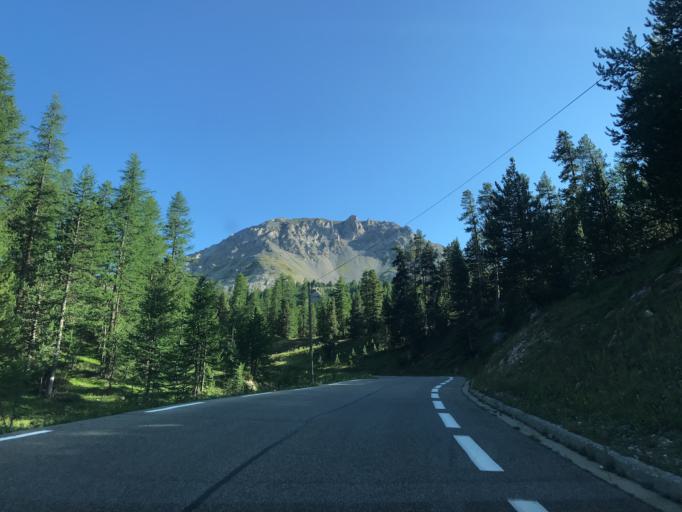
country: FR
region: Provence-Alpes-Cote d'Azur
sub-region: Departement des Hautes-Alpes
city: Villar-Saint-Pancrace
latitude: 44.8315
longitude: 6.7243
